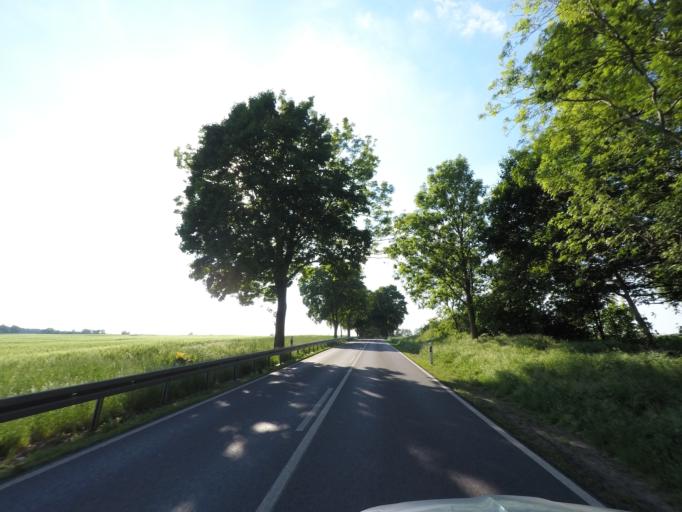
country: DE
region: Brandenburg
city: Hohenfinow
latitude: 52.8148
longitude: 13.9116
